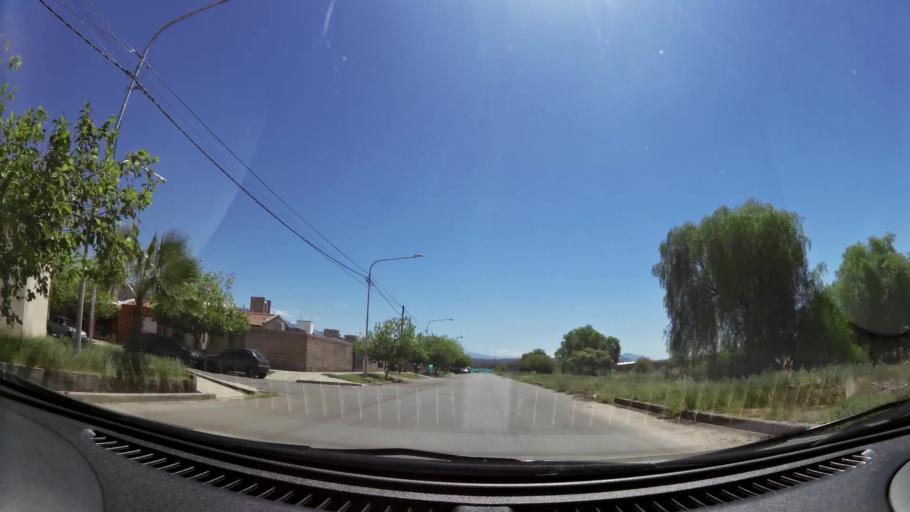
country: AR
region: Mendoza
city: Las Heras
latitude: -32.8395
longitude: -68.8624
